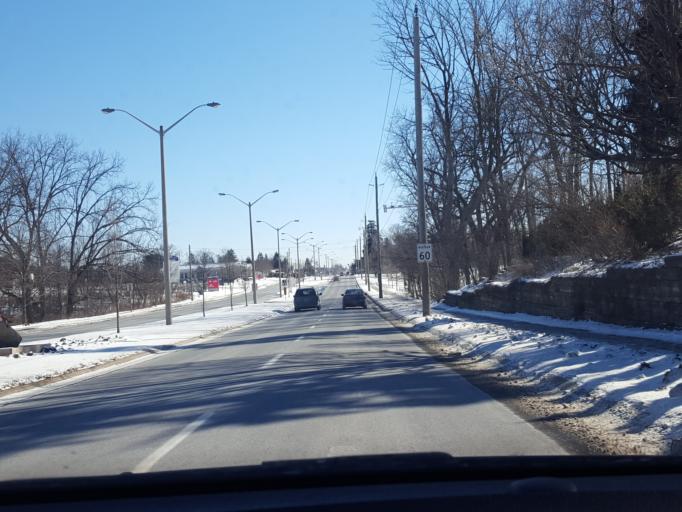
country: CA
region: Ontario
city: Cambridge
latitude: 43.3822
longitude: -80.3336
